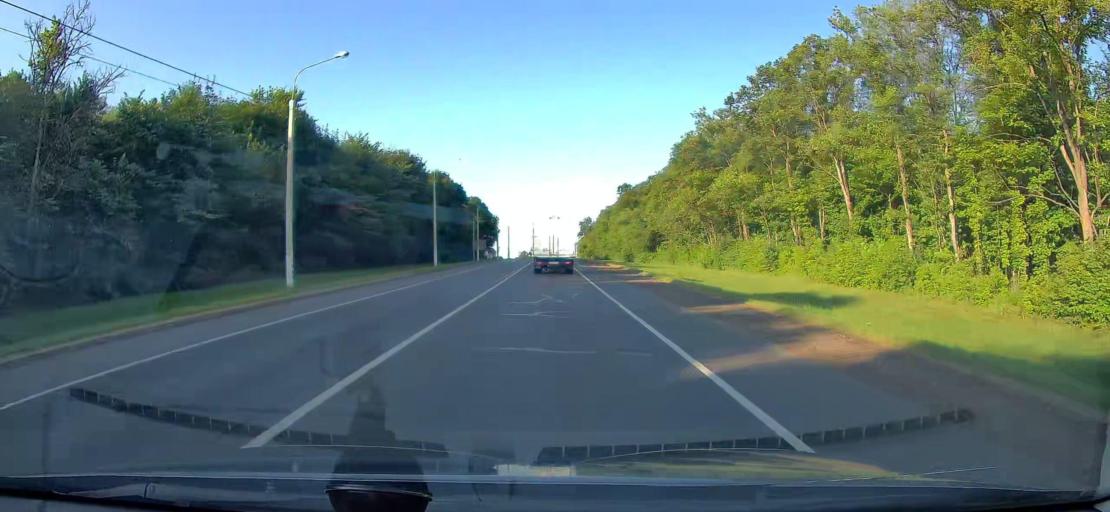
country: RU
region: Tula
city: Plavsk
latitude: 53.8188
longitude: 37.3986
